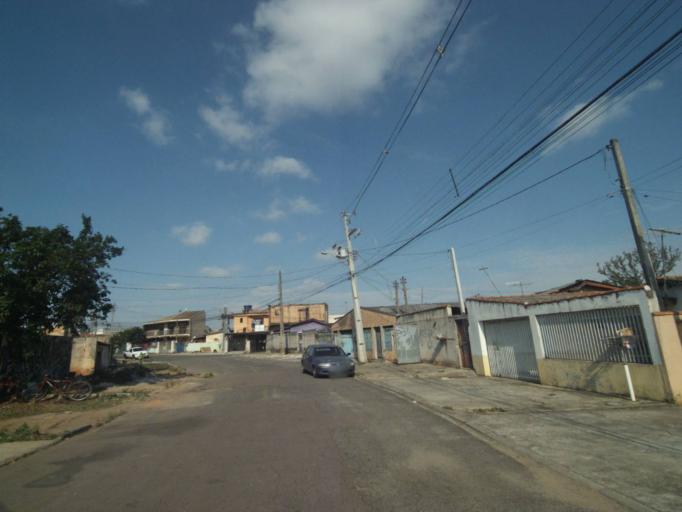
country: BR
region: Parana
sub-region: Curitiba
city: Curitiba
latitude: -25.4906
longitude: -49.3330
